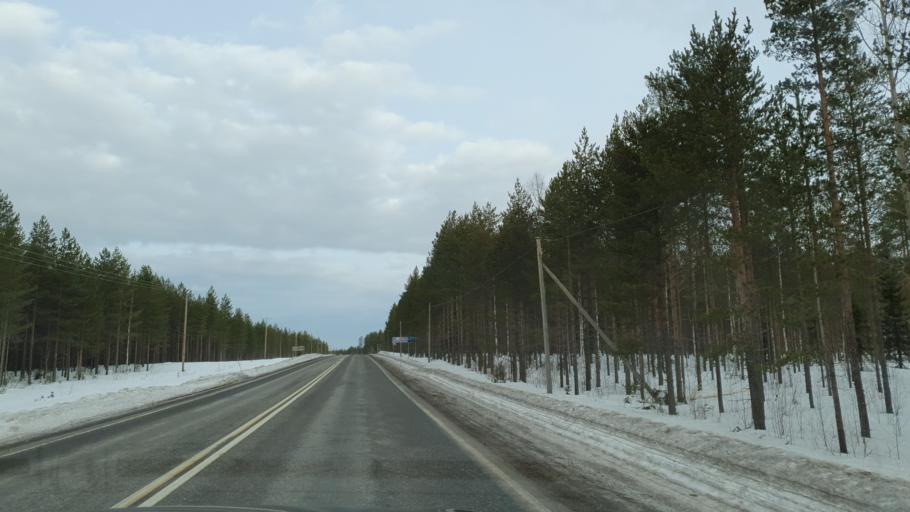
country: FI
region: Kainuu
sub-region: Kajaani
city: Vuokatti
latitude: 64.2125
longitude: 28.1350
